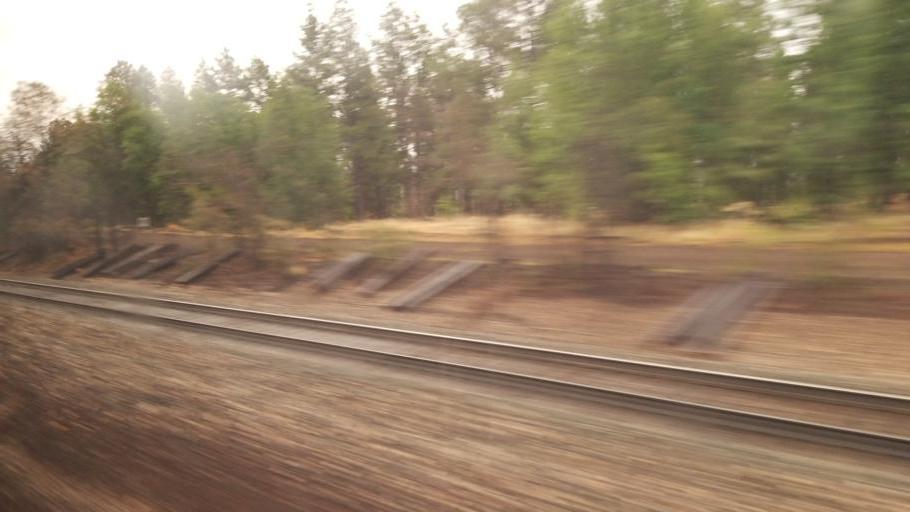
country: US
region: Arizona
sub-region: Coconino County
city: Parks
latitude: 35.2522
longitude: -111.9433
